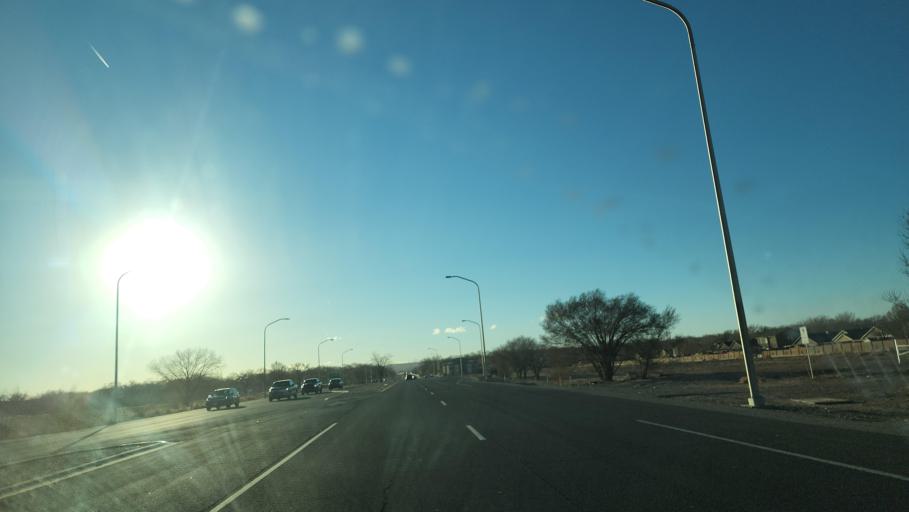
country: US
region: New Mexico
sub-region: Bernalillo County
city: South Valley
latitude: 35.0273
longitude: -106.6616
